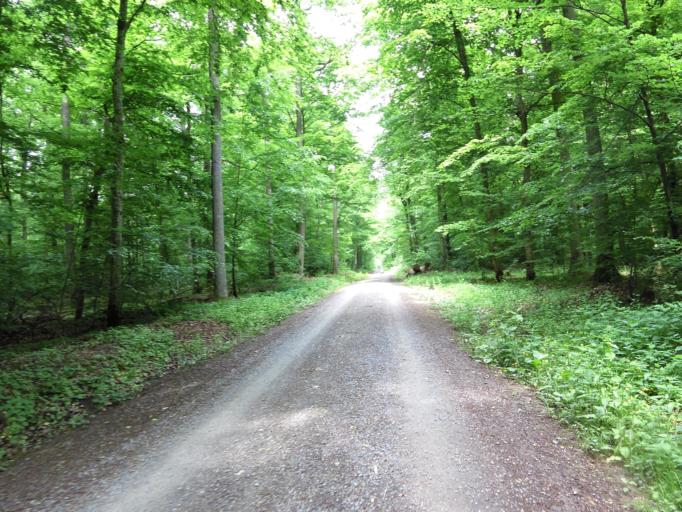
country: DE
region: Bavaria
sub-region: Regierungsbezirk Unterfranken
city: Kleinrinderfeld
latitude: 49.7204
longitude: 9.8300
